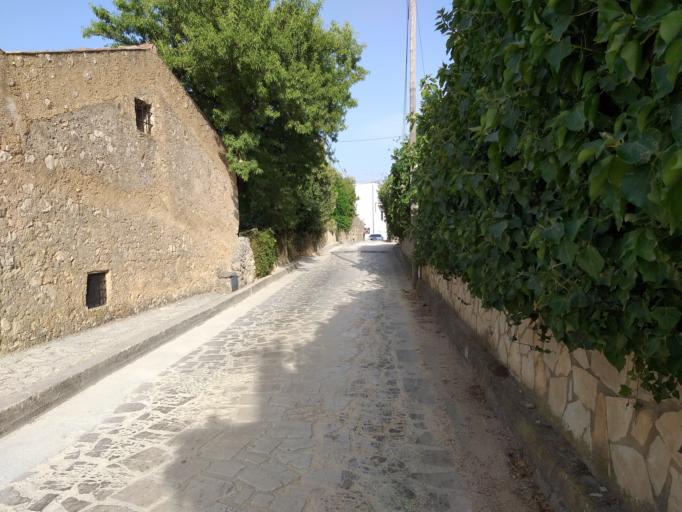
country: IT
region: Sicily
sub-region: Trapani
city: Castelluzzo
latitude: 38.0711
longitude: 12.8164
